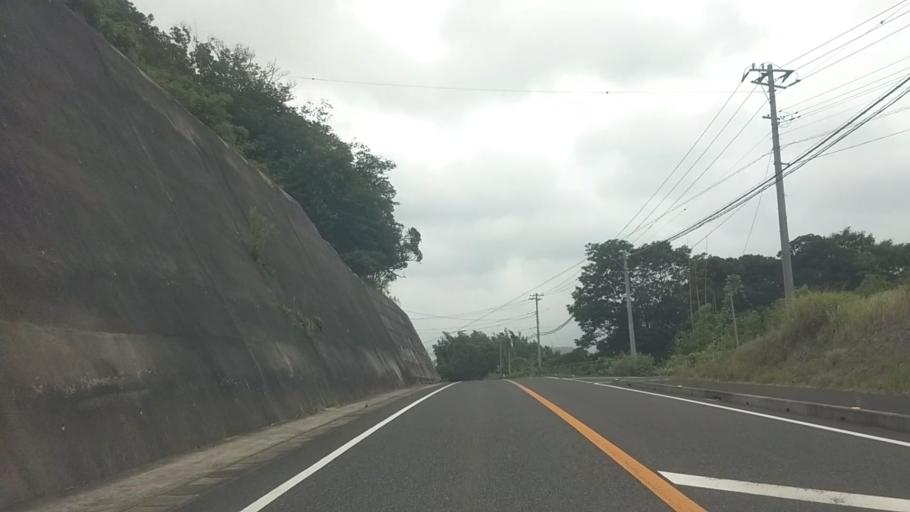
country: JP
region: Chiba
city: Kimitsu
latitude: 35.2195
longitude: 139.9359
